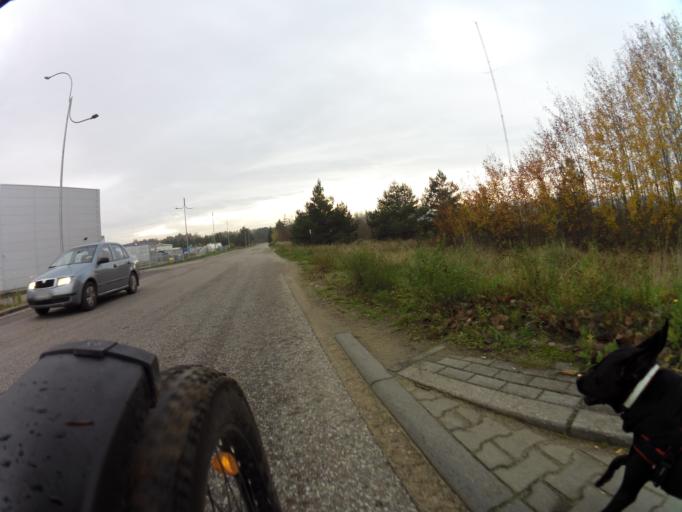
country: PL
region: Pomeranian Voivodeship
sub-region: Powiat pucki
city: Krokowa
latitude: 54.7382
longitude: 18.0941
